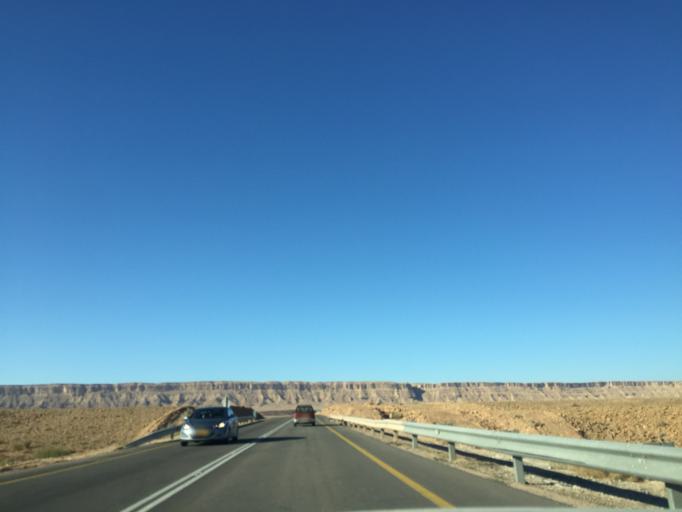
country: IL
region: Southern District
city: Mitzpe Ramon
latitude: 30.6067
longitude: 34.8645
